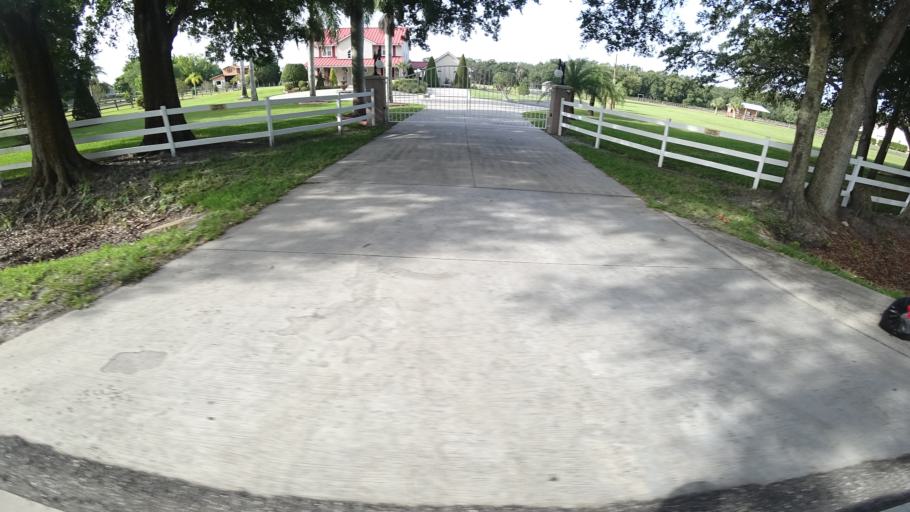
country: US
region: Florida
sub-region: Manatee County
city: Ellenton
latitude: 27.5469
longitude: -82.5245
